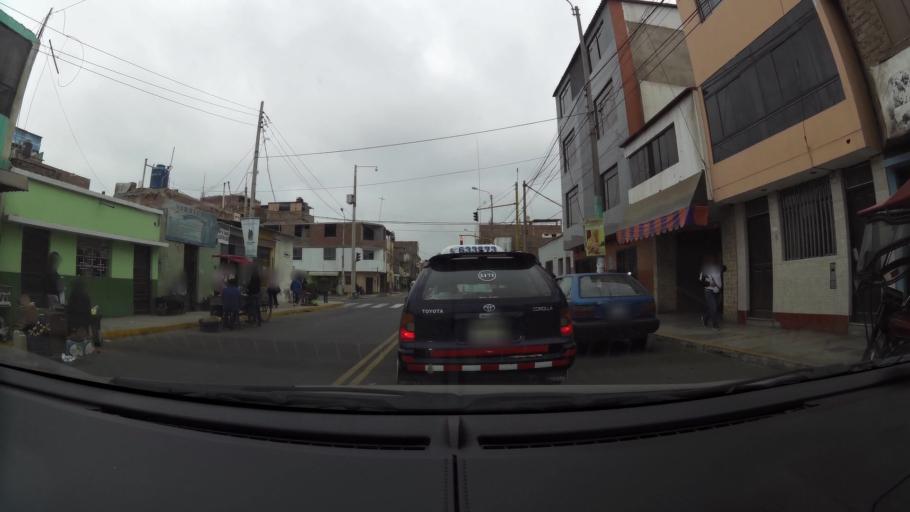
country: PE
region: La Libertad
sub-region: Provincia de Trujillo
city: Trujillo
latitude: -8.1215
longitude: -79.0238
